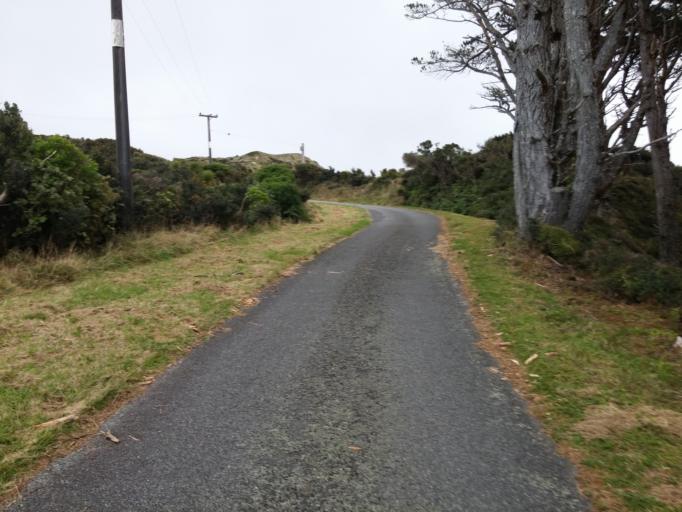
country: NZ
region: Wellington
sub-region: Wellington City
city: Brooklyn
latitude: -41.3210
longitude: 174.7320
